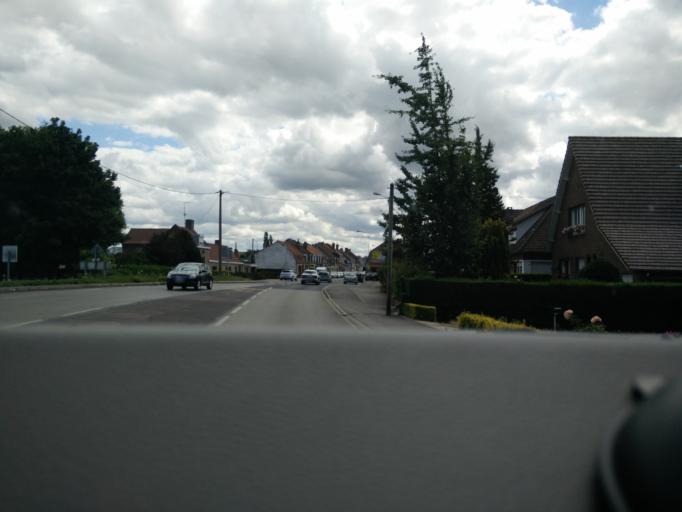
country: FR
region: Nord-Pas-de-Calais
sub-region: Departement du Nord
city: Bergues
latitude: 50.9624
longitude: 2.4330
